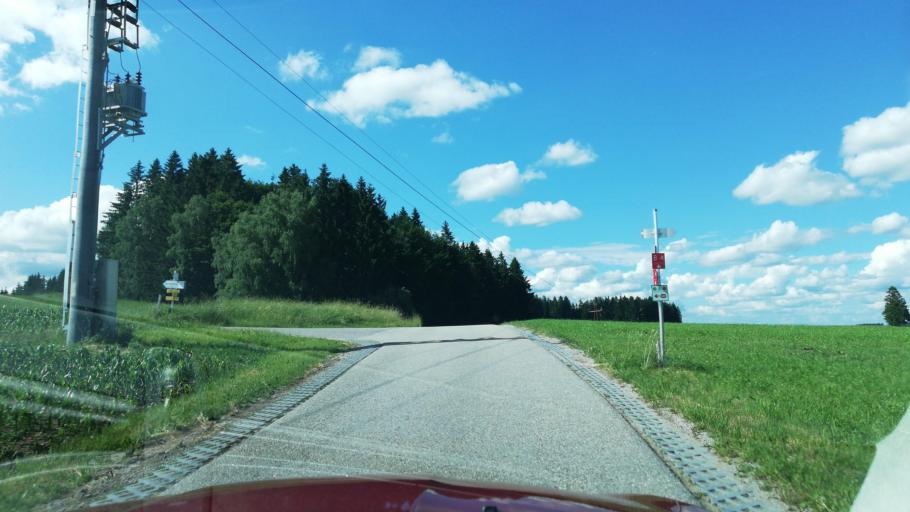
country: AT
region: Upper Austria
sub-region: Politischer Bezirk Urfahr-Umgebung
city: Sonnberg im Muehlkreis
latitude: 48.4615
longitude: 14.3280
